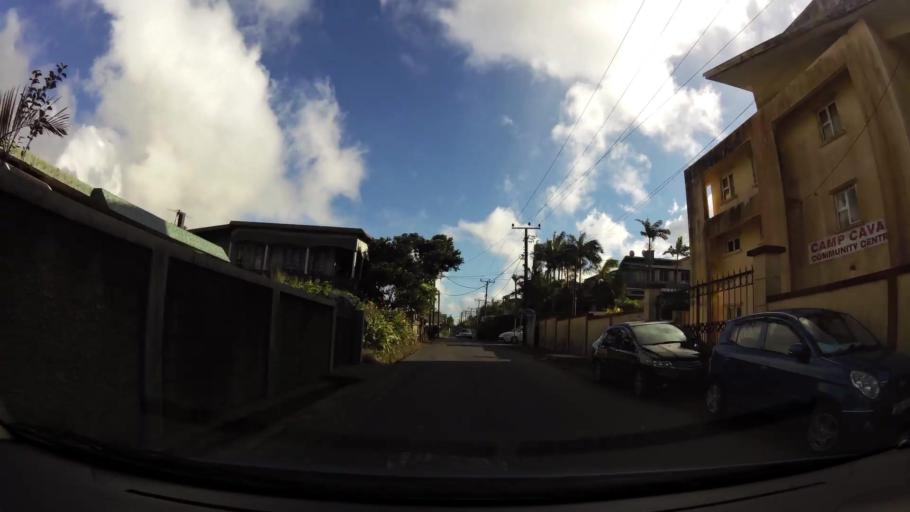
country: MU
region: Plaines Wilhems
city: Curepipe
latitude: -20.3219
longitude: 57.5126
